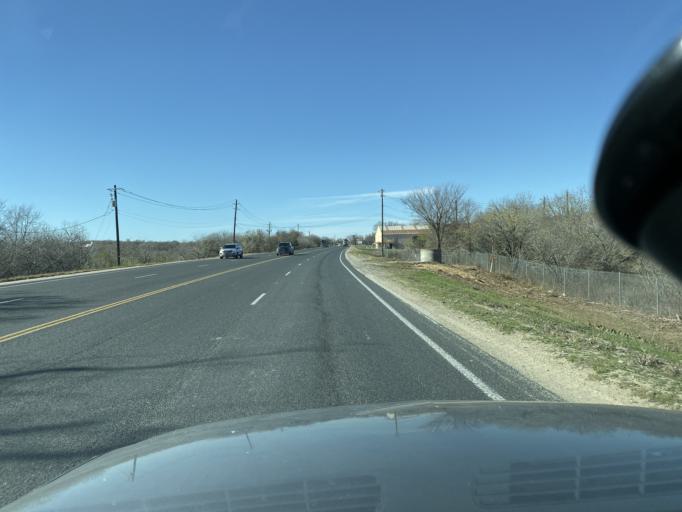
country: US
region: Texas
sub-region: Travis County
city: Garfield
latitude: 30.1710
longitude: -97.6653
